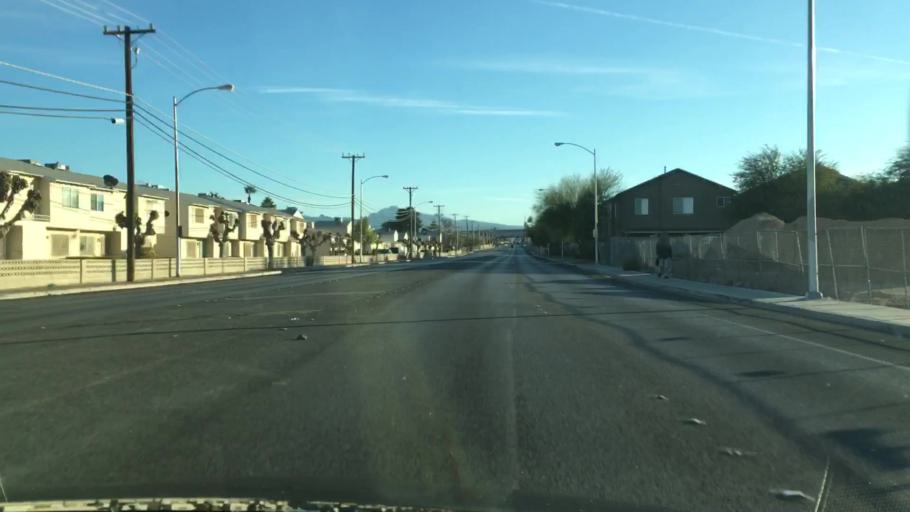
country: US
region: Nevada
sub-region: Clark County
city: Whitney
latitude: 36.0991
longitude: -115.0733
